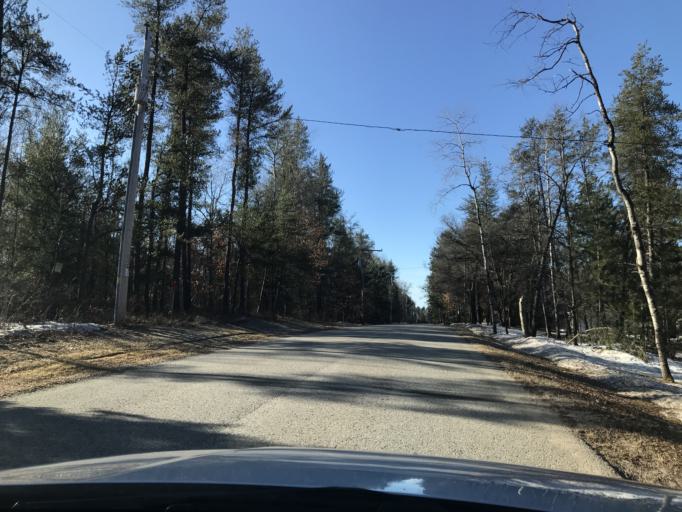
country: US
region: Michigan
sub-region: Dickinson County
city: Kingsford
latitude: 45.3917
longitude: -88.1613
